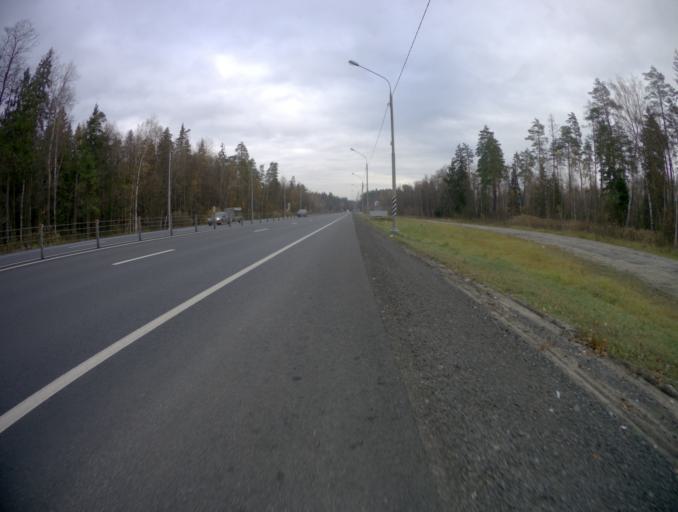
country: RU
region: Moskovskaya
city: Malaya Dubna
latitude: 55.8590
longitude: 38.9626
